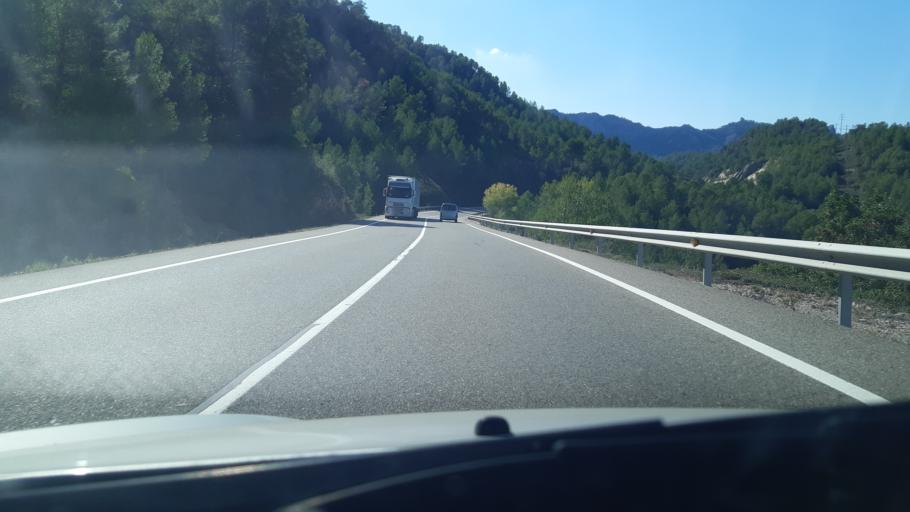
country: ES
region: Catalonia
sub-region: Provincia de Tarragona
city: Rasquera
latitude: 40.9997
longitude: 0.5799
